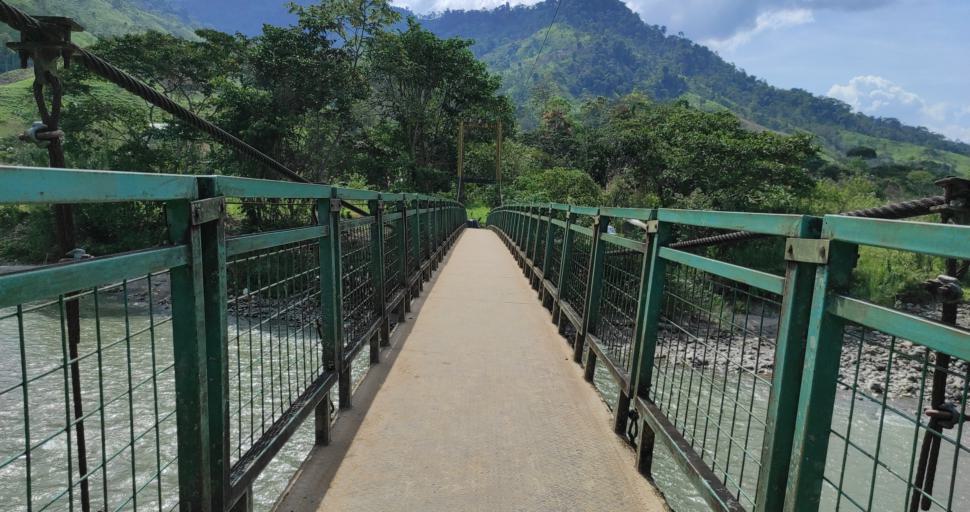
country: EC
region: Zamora-Chinchipe
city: Yantzaza
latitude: -3.7852
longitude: -78.9032
